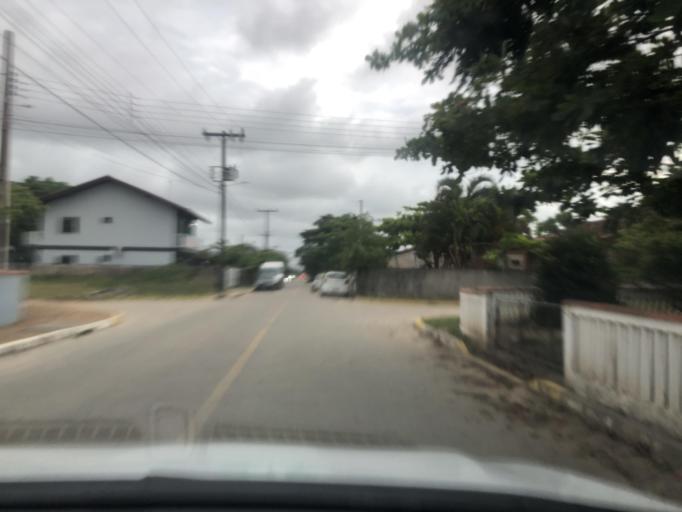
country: BR
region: Santa Catarina
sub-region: Sao Francisco Do Sul
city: Sao Francisco do Sul
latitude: -26.2336
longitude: -48.5194
